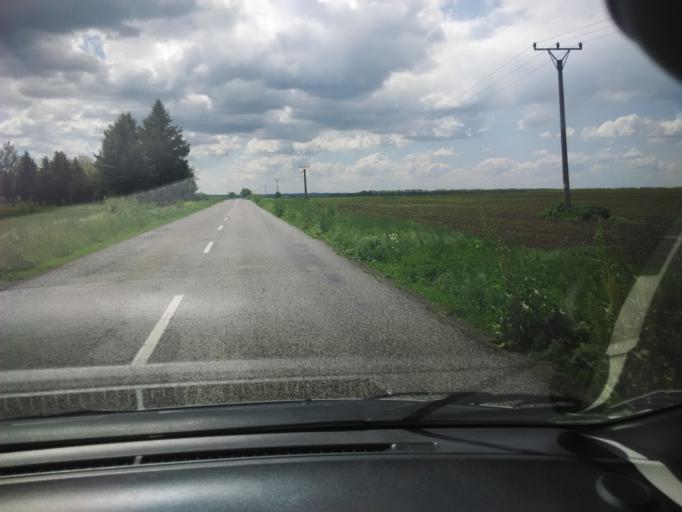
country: SK
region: Nitriansky
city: Levice
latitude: 48.1598
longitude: 18.5480
